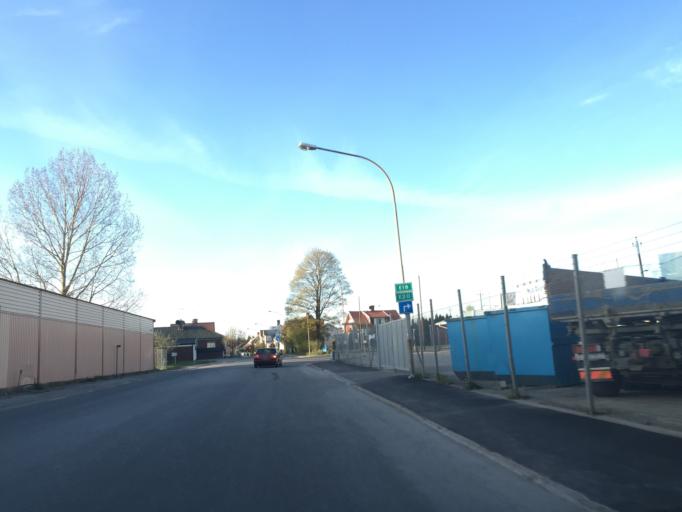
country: SE
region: OErebro
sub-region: Orebro Kommun
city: Orebro
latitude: 59.2888
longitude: 15.2186
